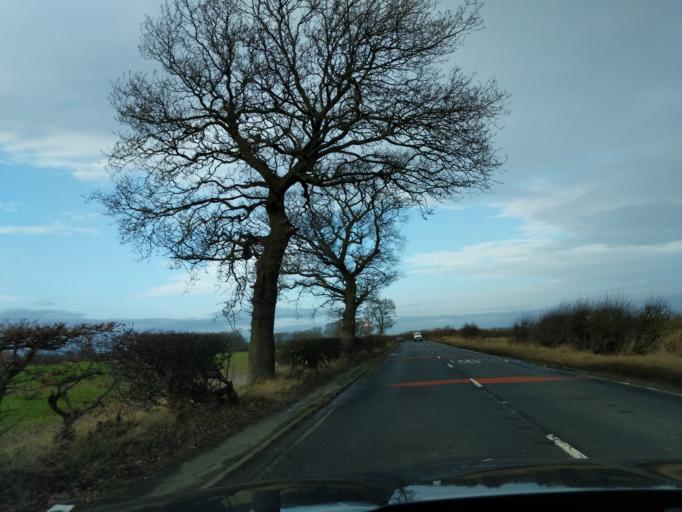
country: GB
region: England
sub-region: Northumberland
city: Ponteland
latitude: 55.0513
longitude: -1.7575
